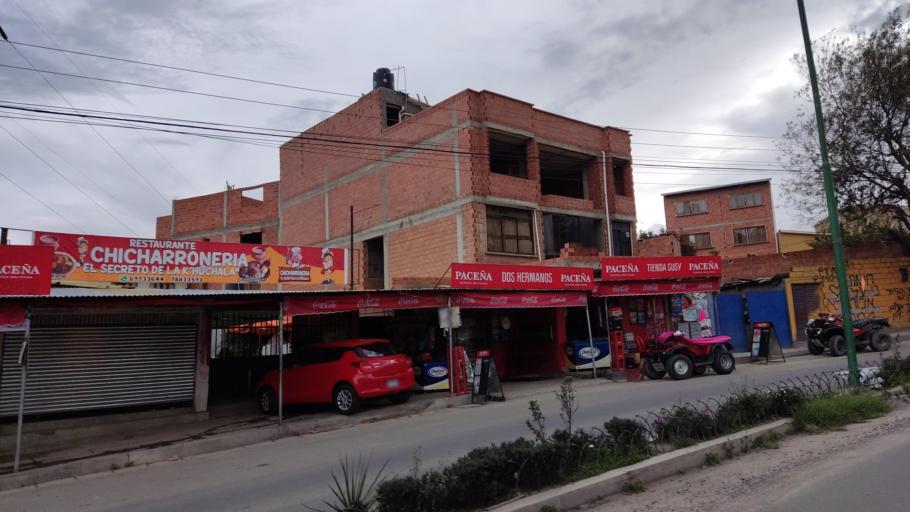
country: BO
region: La Paz
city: La Paz
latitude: -16.5674
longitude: -68.0908
